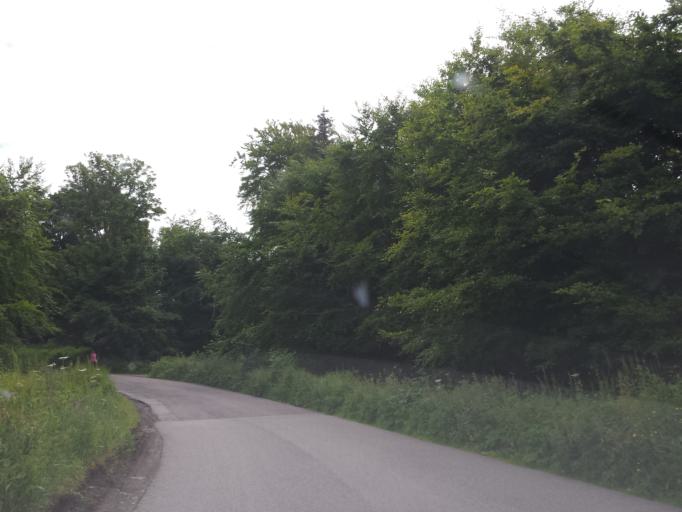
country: GB
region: Scotland
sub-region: Argyll and Bute
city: Oban
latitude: 56.4483
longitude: -5.4455
